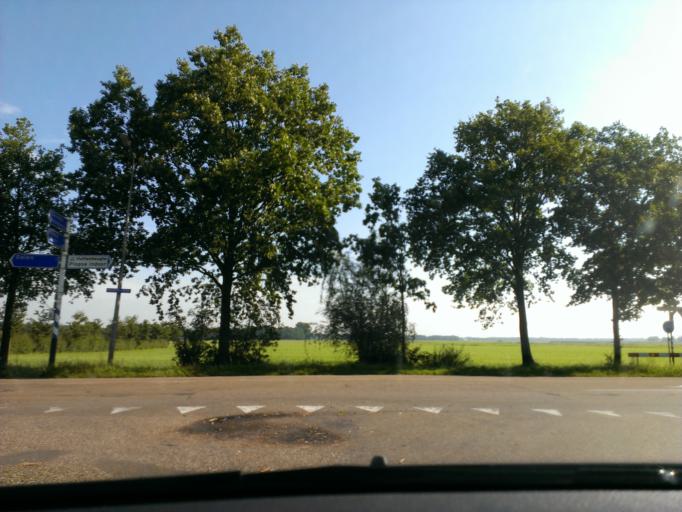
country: NL
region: Drenthe
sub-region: Gemeente Coevorden
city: Dalen
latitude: 52.6815
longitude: 6.7656
